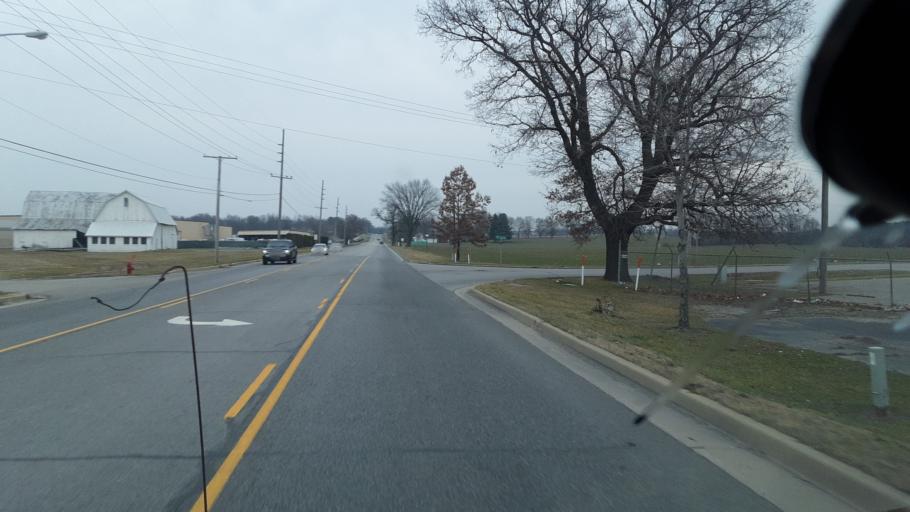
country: US
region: Indiana
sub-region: Elkhart County
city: Middlebury
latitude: 41.6868
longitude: -85.6994
